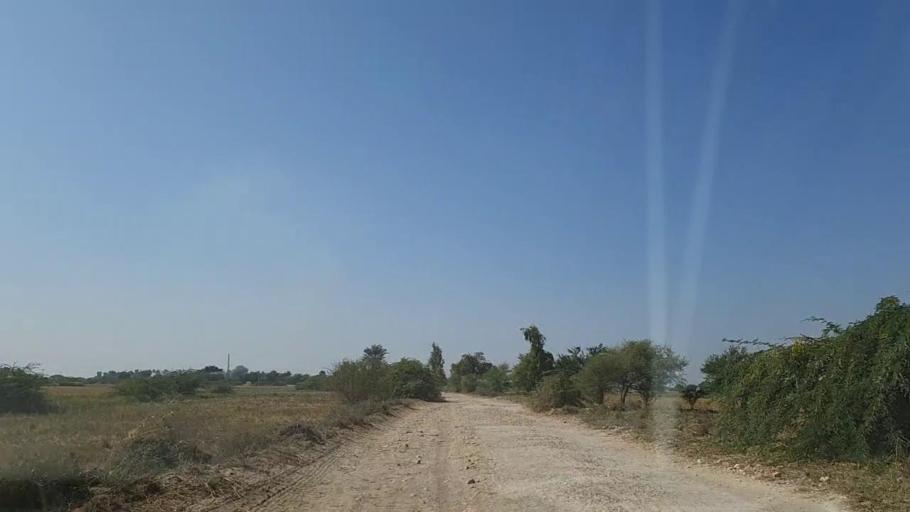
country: PK
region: Sindh
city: Chuhar Jamali
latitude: 24.4243
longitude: 68.0050
